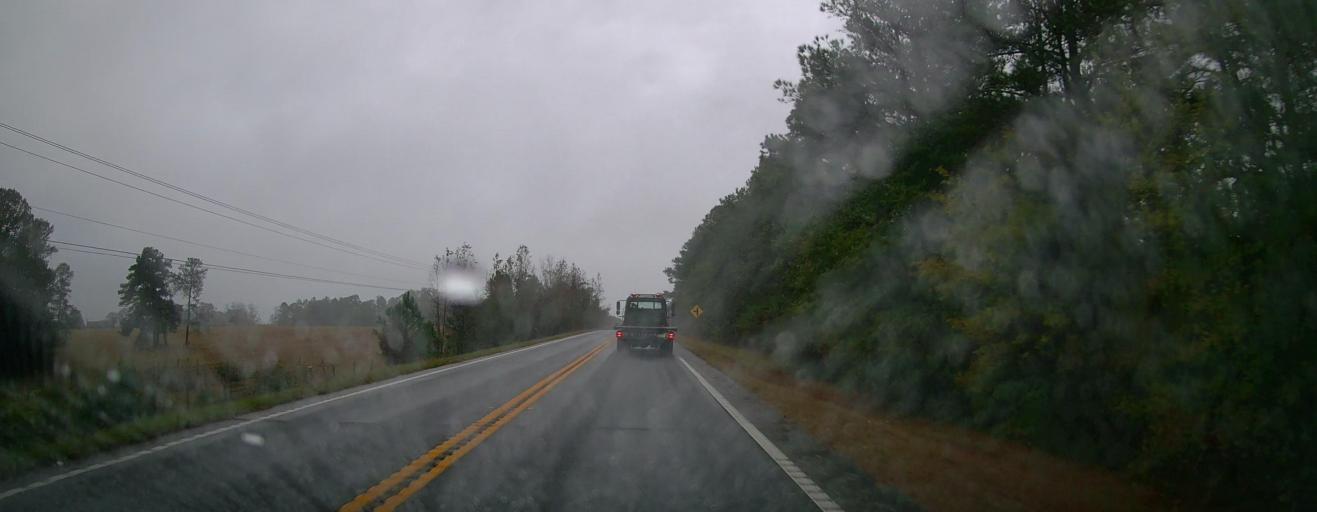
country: US
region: Georgia
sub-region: Jones County
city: Gray
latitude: 33.0325
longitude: -83.5175
